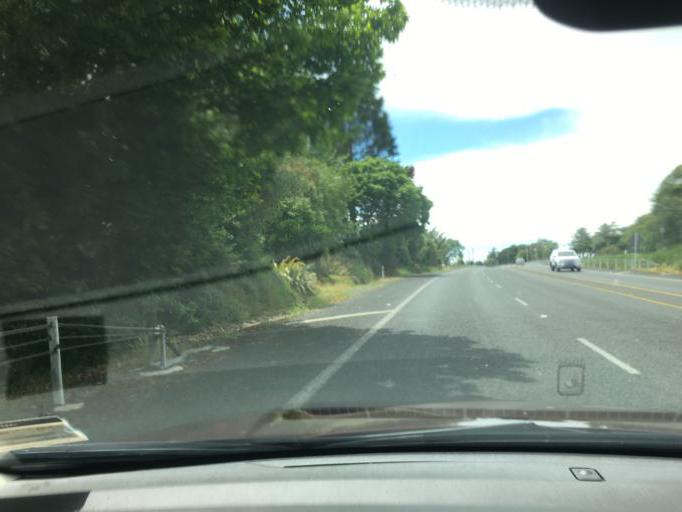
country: NZ
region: Waikato
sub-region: Waipa District
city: Cambridge
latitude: -37.9474
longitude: 175.3133
